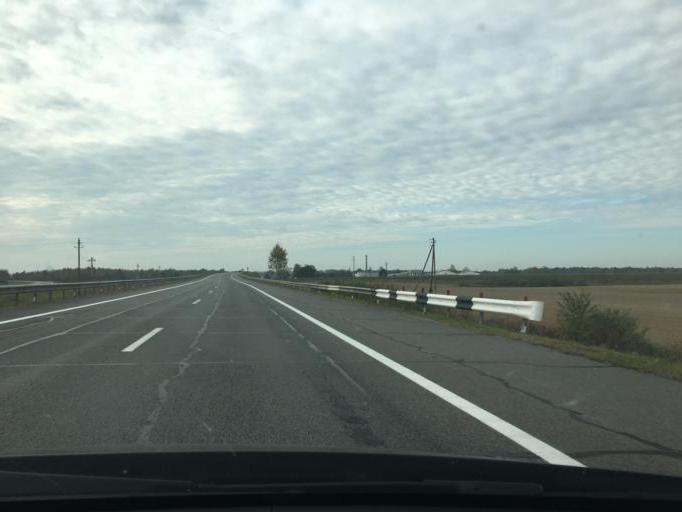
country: BY
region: Minsk
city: Stan'kava
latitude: 53.6778
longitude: 27.1983
